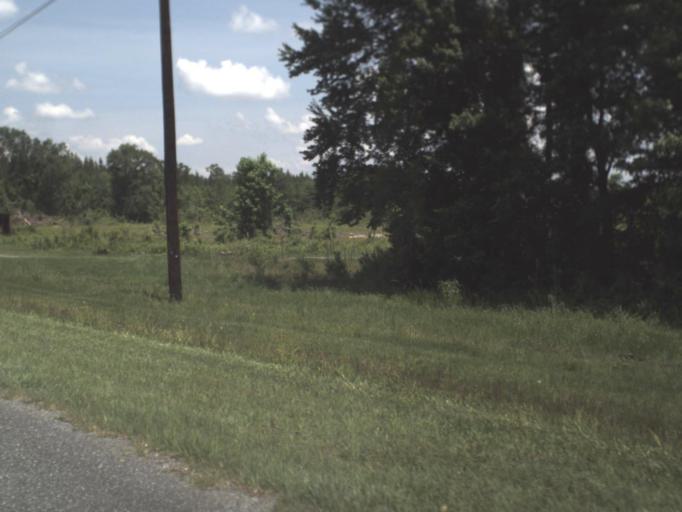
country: US
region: Florida
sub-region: Union County
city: Lake Butler
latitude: 29.9852
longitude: -82.2510
